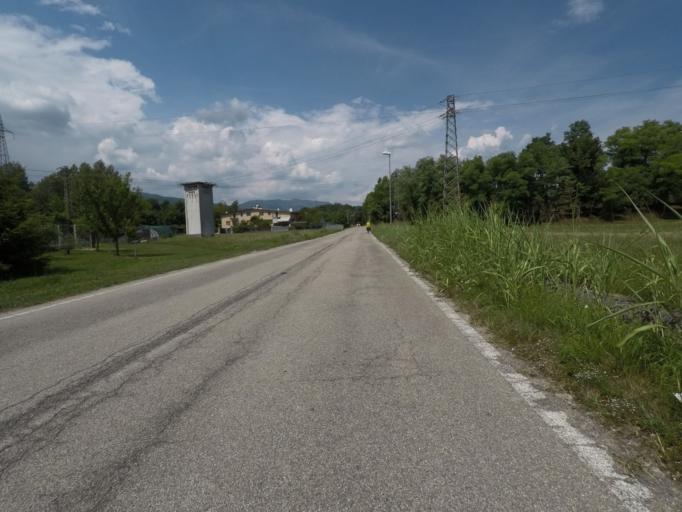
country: IT
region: Friuli Venezia Giulia
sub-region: Provincia di Pordenone
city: Lestans
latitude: 46.1721
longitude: 12.8963
